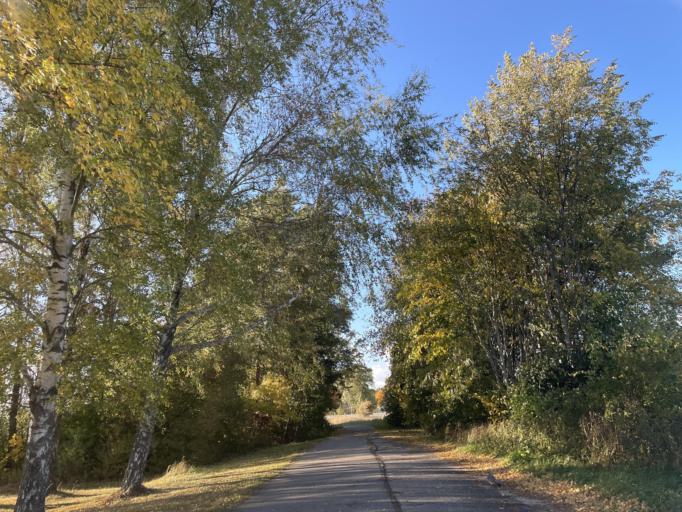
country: SE
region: Soedermanland
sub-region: Eskilstuna Kommun
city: Eskilstuna
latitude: 59.3881
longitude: 16.4995
